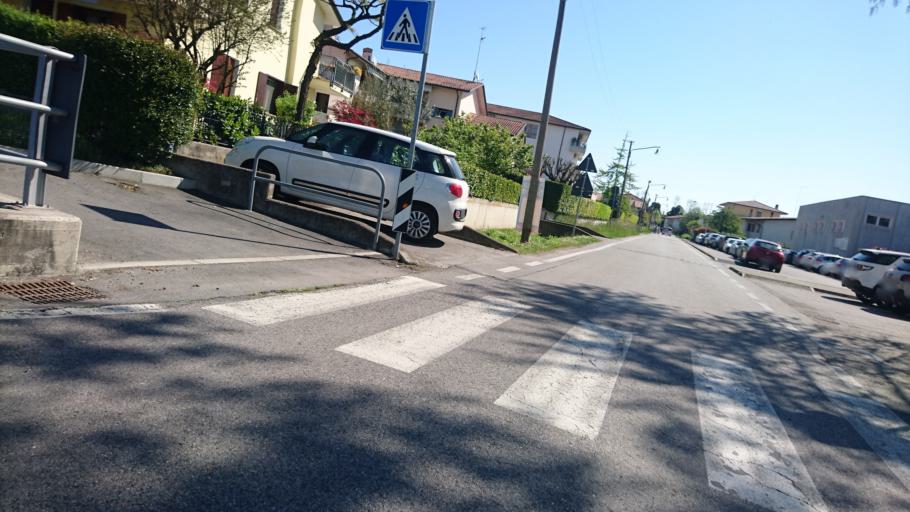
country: IT
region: Veneto
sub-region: Provincia di Treviso
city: Treviso
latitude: 45.6632
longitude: 12.2160
